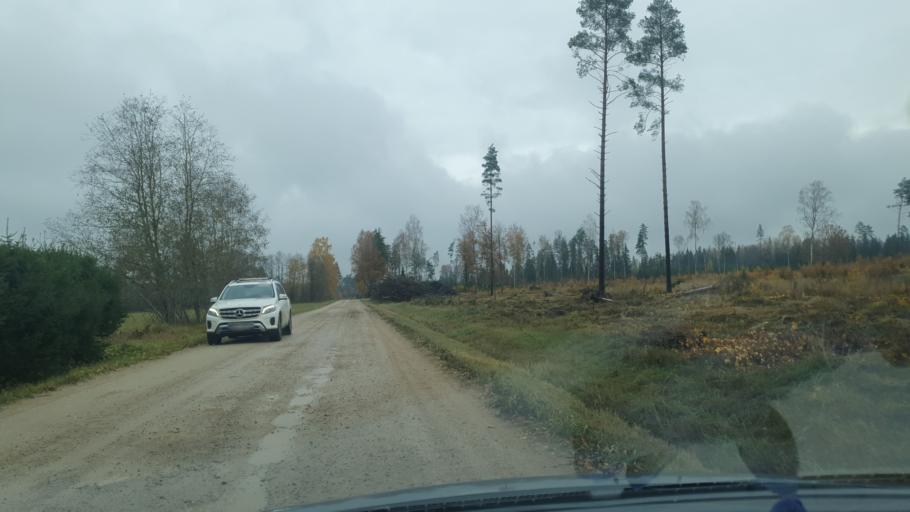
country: EE
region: Viljandimaa
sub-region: Karksi vald
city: Karksi-Nuia
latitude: 58.0092
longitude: 25.6574
